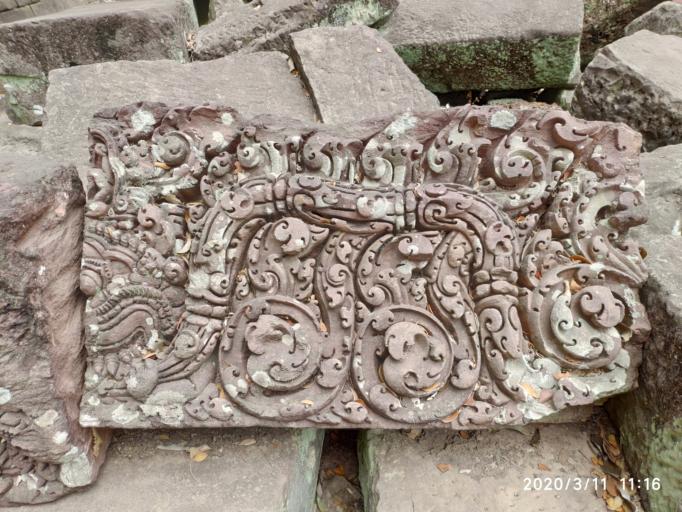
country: KH
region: Siem Reap
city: Siem Reap
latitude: 13.4484
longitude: 103.8605
